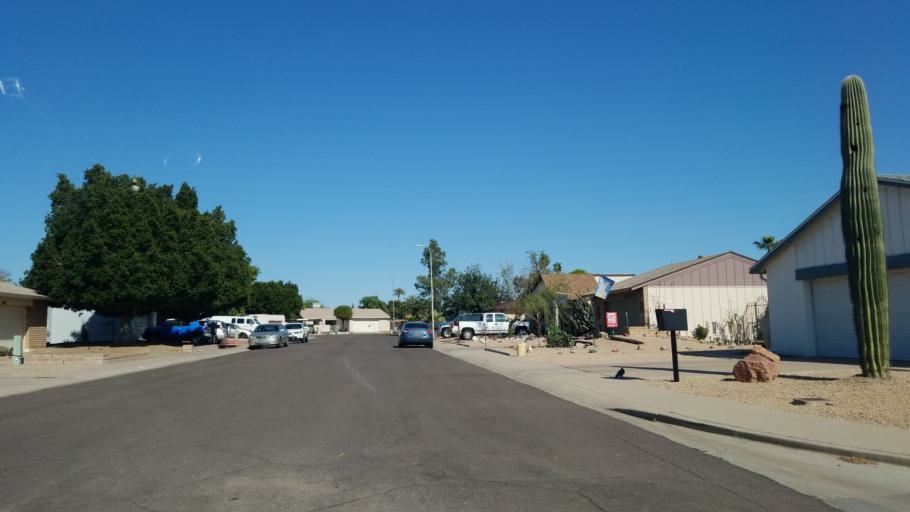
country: US
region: Arizona
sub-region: Maricopa County
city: Glendale
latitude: 33.5739
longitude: -112.1761
